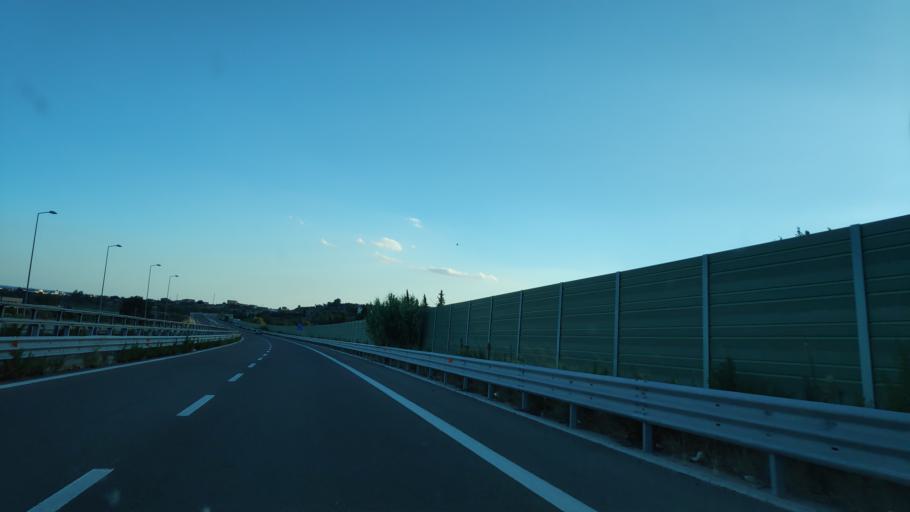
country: IT
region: Calabria
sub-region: Provincia di Reggio Calabria
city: Siderno
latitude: 38.2696
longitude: 16.2678
